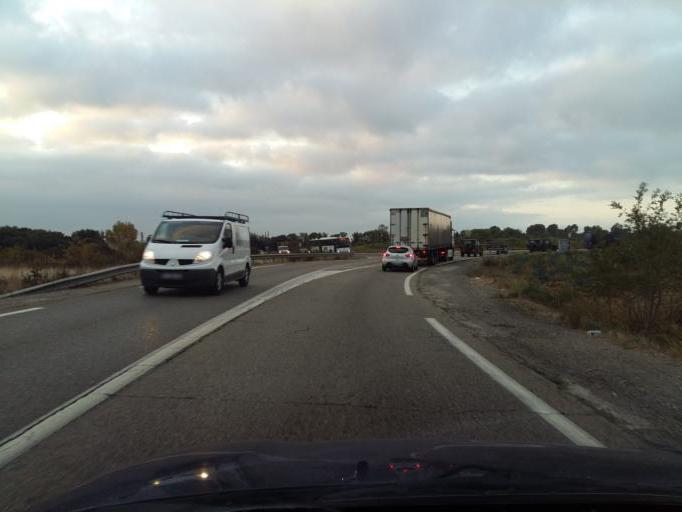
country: FR
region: Provence-Alpes-Cote d'Azur
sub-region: Departement des Bouches-du-Rhone
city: Miramas
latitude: 43.6082
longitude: 5.0105
